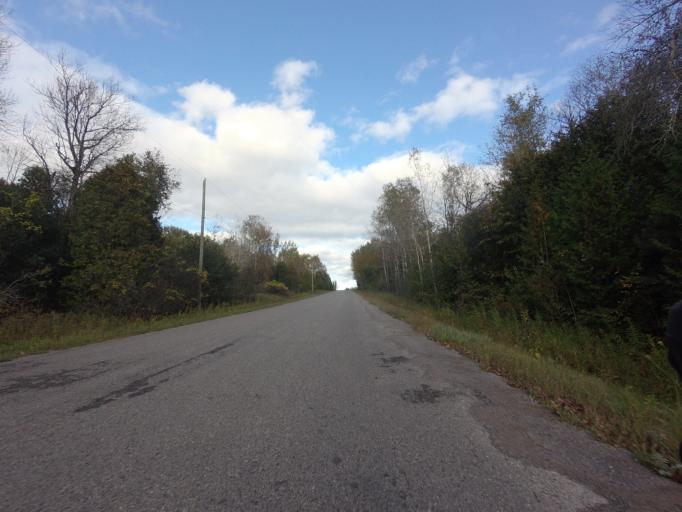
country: CA
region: Ontario
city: Cobourg
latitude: 43.9780
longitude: -77.9986
